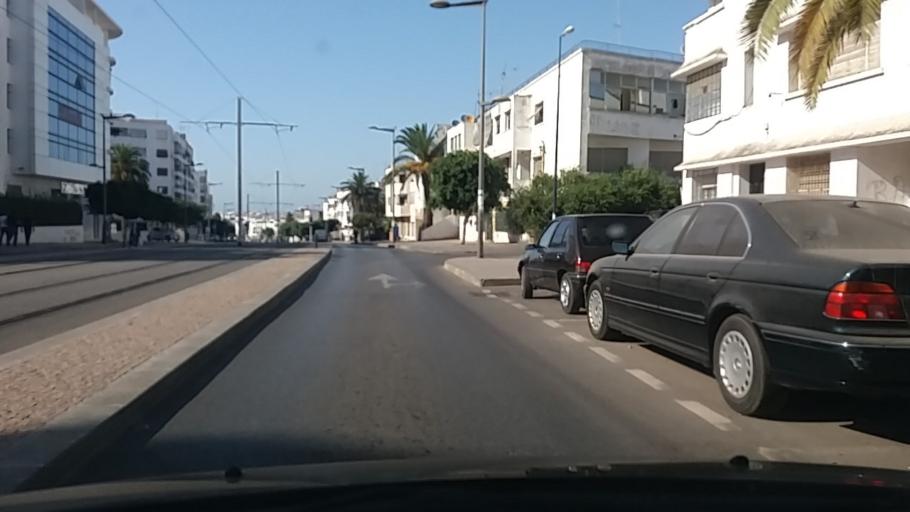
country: MA
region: Rabat-Sale-Zemmour-Zaer
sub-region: Rabat
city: Rabat
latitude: 34.0218
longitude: -6.8250
